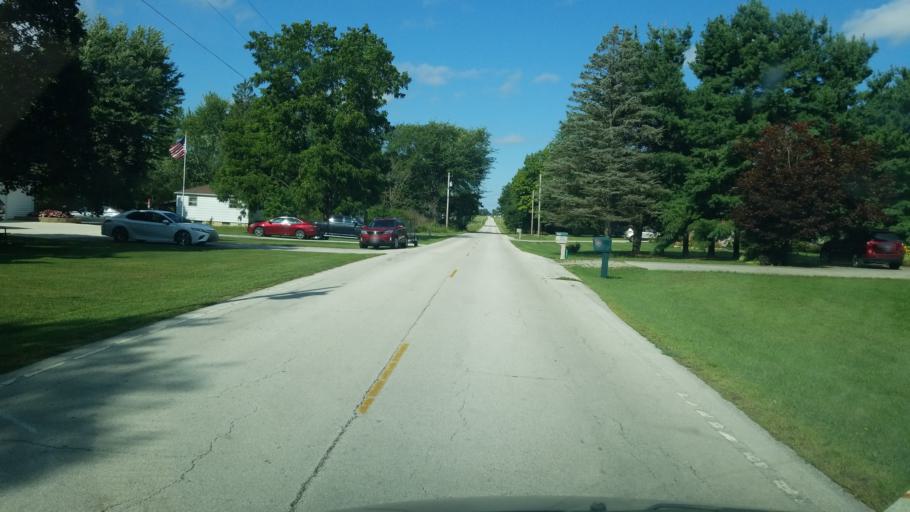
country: US
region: Ohio
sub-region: Seneca County
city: Fostoria
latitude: 41.1081
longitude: -83.4426
